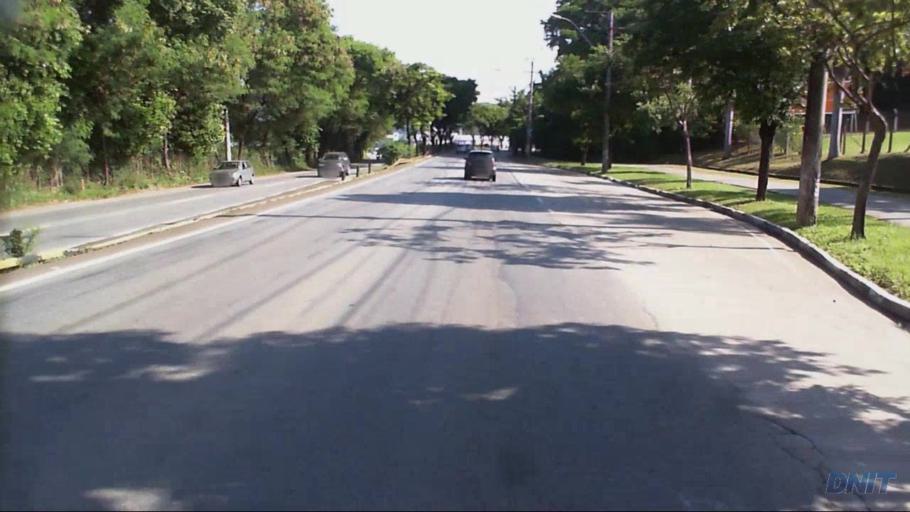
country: BR
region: Minas Gerais
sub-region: Ipatinga
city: Ipatinga
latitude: -19.4893
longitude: -42.5609
